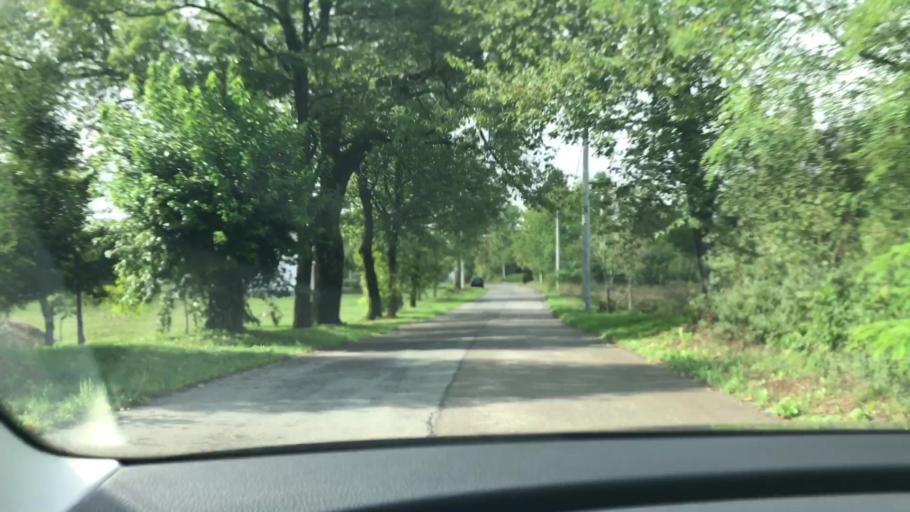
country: BA
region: Federation of Bosnia and Herzegovina
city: Izacic
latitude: 44.8764
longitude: 15.7155
